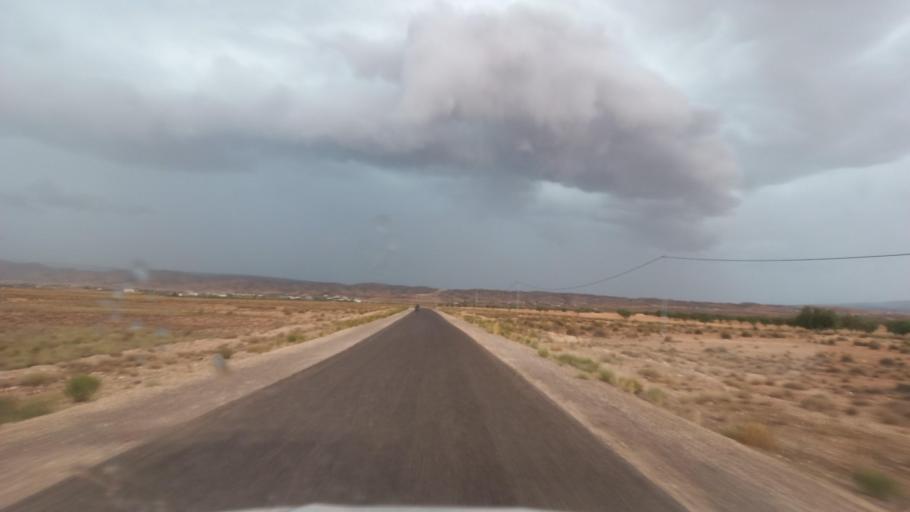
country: TN
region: Al Qasrayn
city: Sbiba
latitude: 35.3280
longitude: 9.0125
